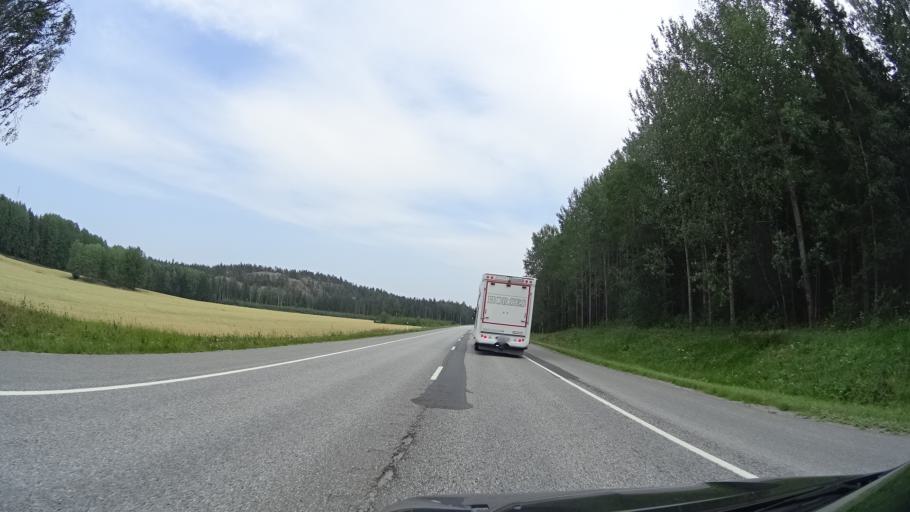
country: FI
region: Uusimaa
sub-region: Raaseporin
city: Karis
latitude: 60.0767
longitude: 23.7516
